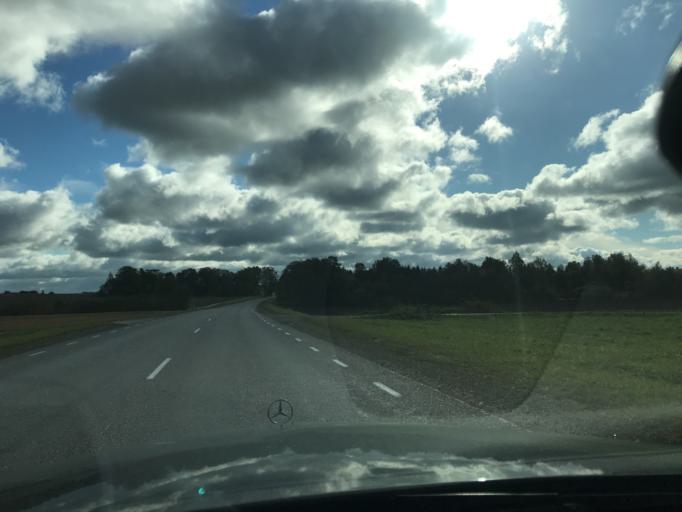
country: EE
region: Vorumaa
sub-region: Antsla vald
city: Vana-Antsla
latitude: 57.9431
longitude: 26.3032
